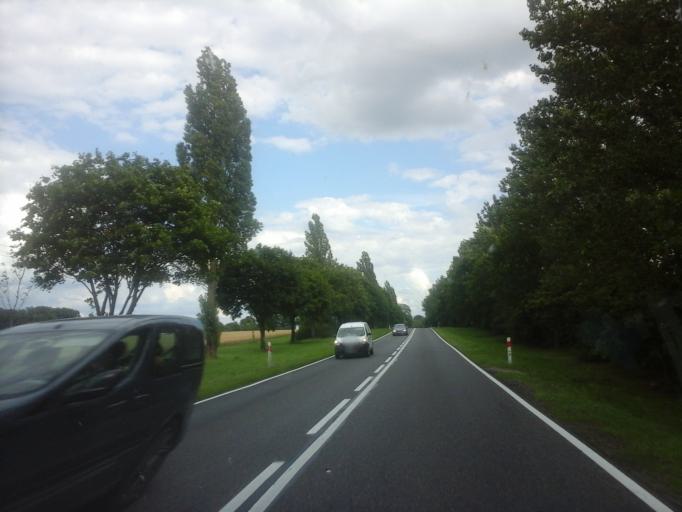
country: PL
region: West Pomeranian Voivodeship
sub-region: Powiat stargardzki
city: Stargard Szczecinski
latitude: 53.3050
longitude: 15.1528
